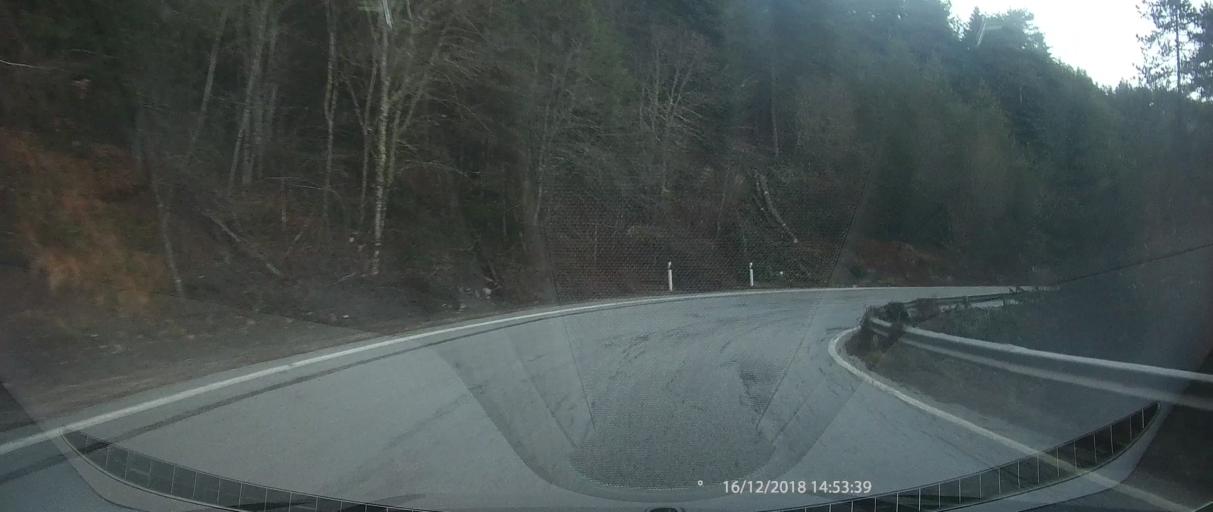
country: GR
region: West Macedonia
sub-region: Nomos Kastorias
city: Nestorio
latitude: 40.2108
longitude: 21.0563
